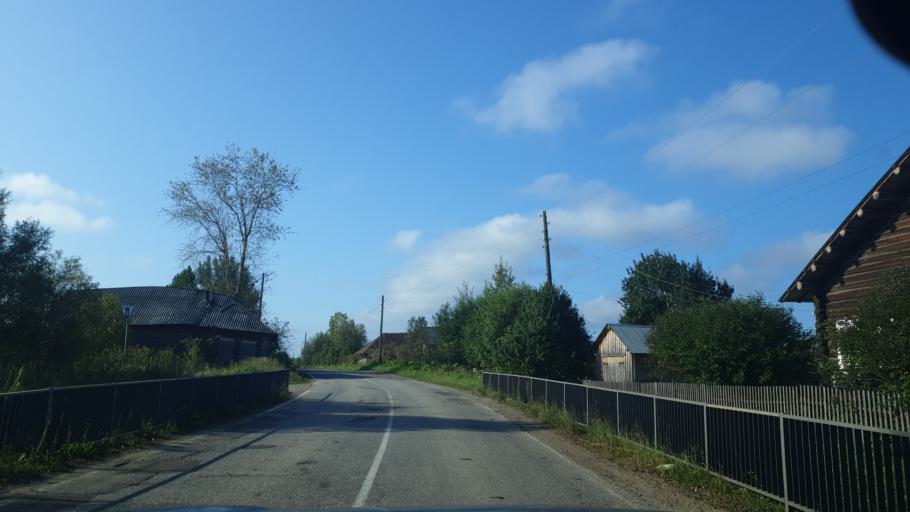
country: RU
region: Komi Republic
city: Vizinga
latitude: 60.9391
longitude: 50.2320
